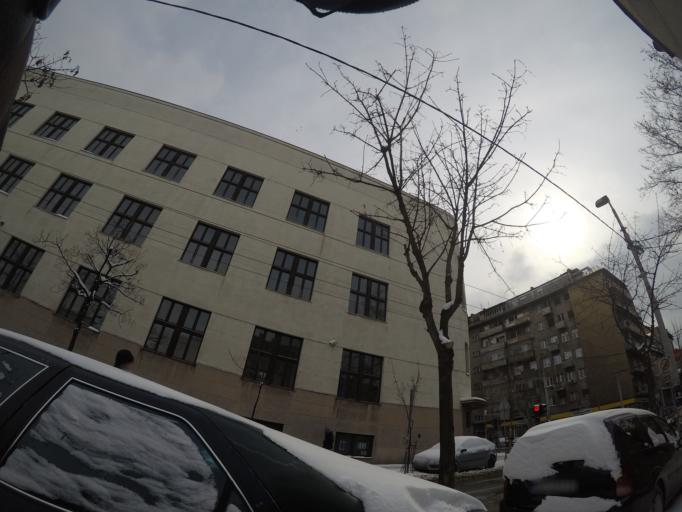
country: RS
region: Central Serbia
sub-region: Belgrade
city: Stari Grad
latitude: 44.8212
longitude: 20.4649
